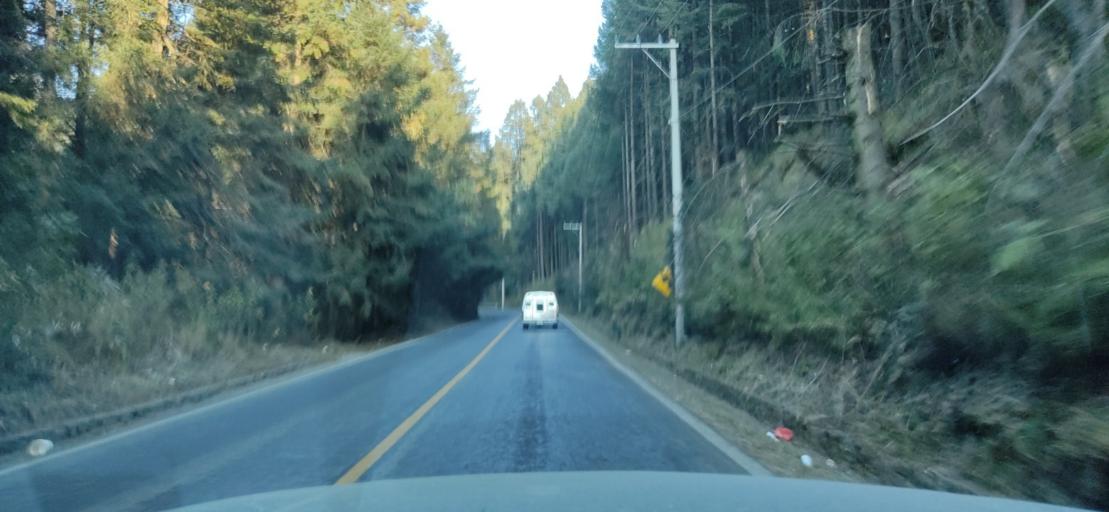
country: MX
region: Mexico
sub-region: Ocoyoacac
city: San Jeronimo Acazulco
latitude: 19.2609
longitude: -99.3738
